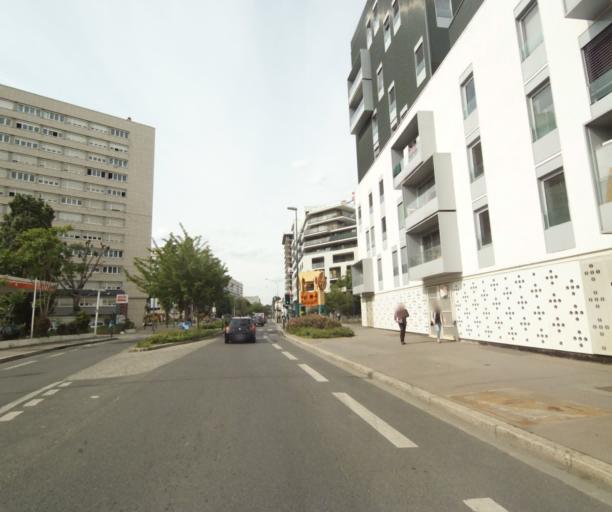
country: FR
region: Ile-de-France
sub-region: Departement des Hauts-de-Seine
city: Asnieres-sur-Seine
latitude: 48.9206
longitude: 2.2952
